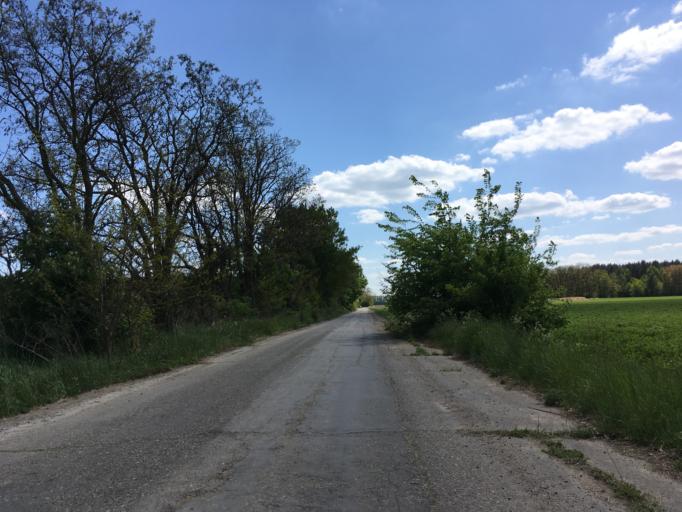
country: DE
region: Brandenburg
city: Rudnitz
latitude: 52.6792
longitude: 13.6728
